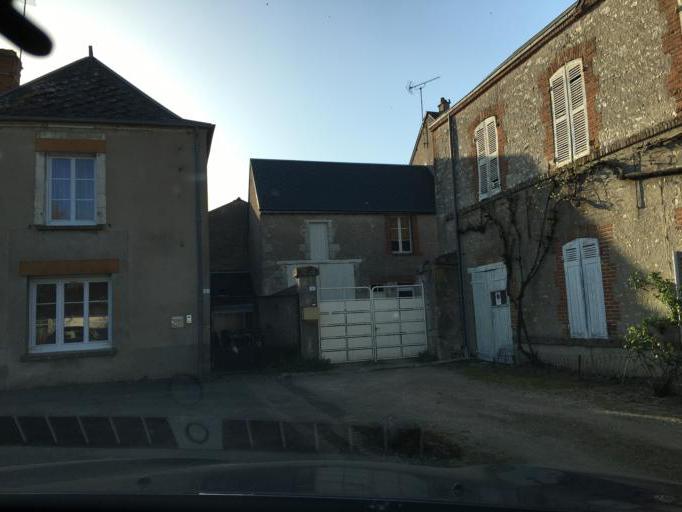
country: FR
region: Centre
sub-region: Departement du Loir-et-Cher
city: Ouzouer-le-Marche
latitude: 47.9105
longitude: 1.5278
